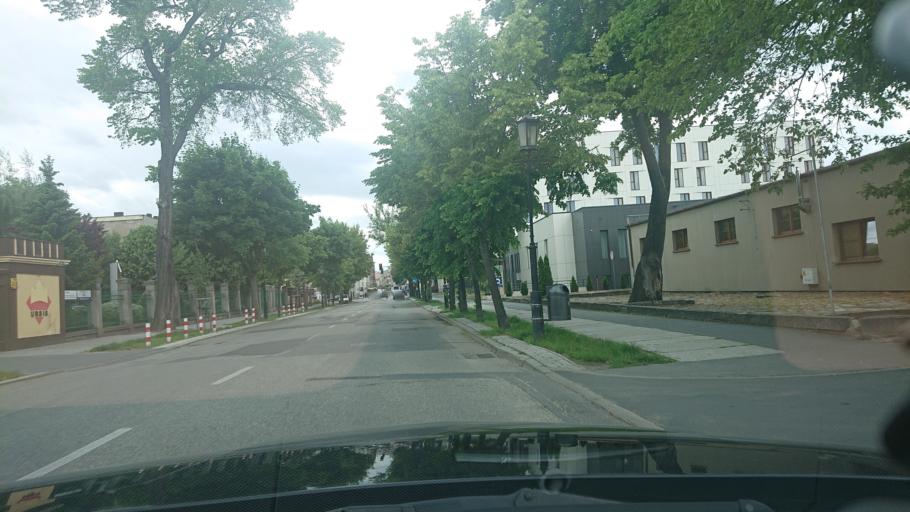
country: PL
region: Greater Poland Voivodeship
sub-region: Powiat gnieznienski
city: Gniezno
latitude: 52.5324
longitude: 17.6050
